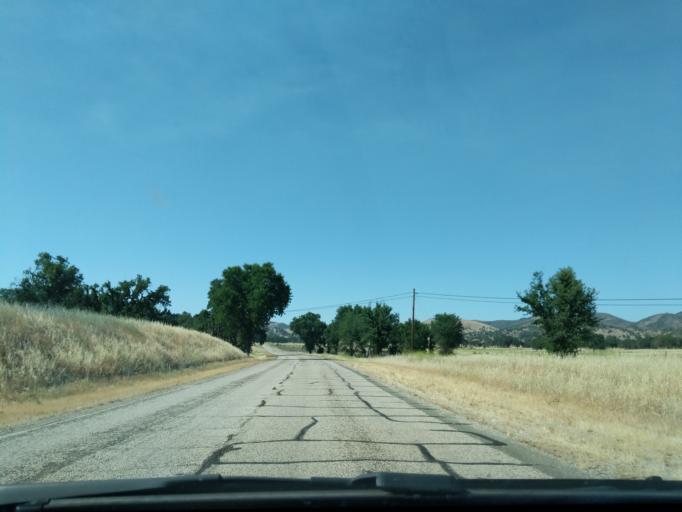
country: US
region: California
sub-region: Monterey County
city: King City
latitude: 36.0221
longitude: -121.1778
